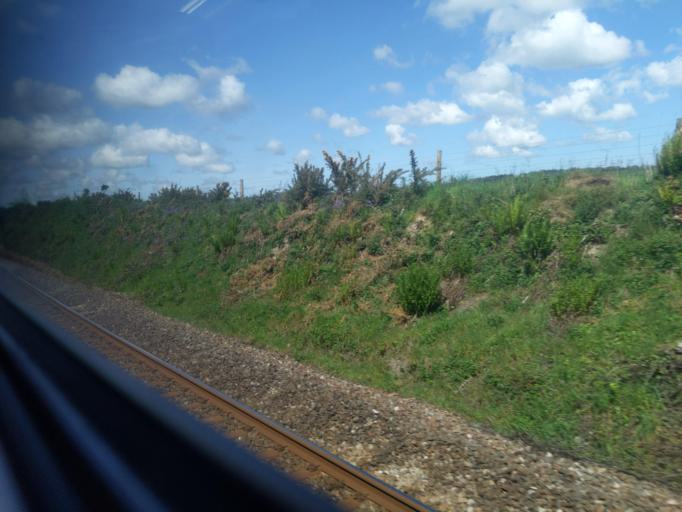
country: GB
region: England
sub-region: Cornwall
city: Liskeard
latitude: 50.4501
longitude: -4.4904
